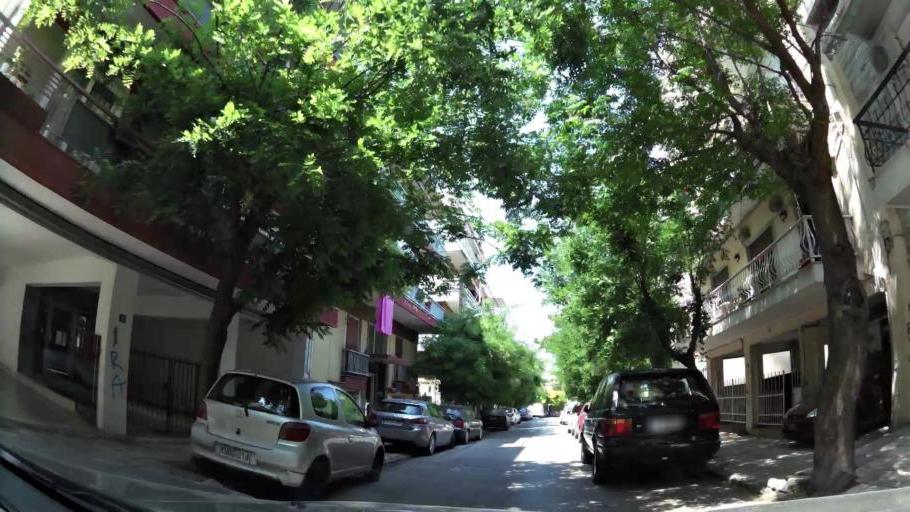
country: GR
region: Central Macedonia
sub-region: Nomos Thessalonikis
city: Agios Pavlos
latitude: 40.6333
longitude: 22.9653
